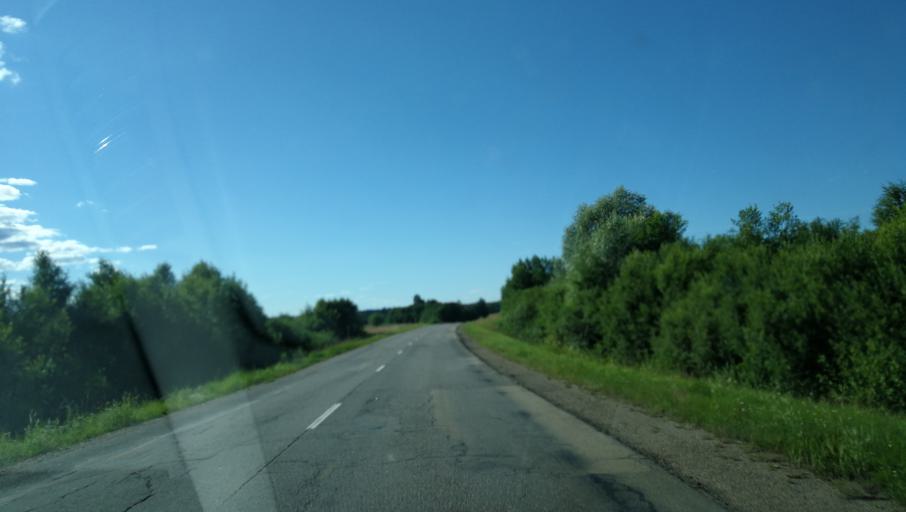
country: LV
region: Jaunpiebalga
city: Jaunpiebalga
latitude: 56.9854
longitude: 26.0209
